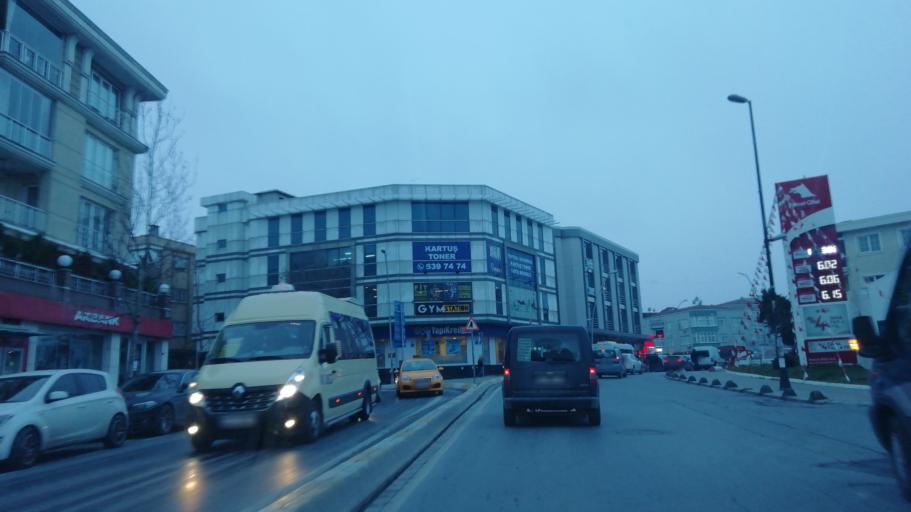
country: TR
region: Istanbul
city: Bahcelievler
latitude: 41.0156
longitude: 28.8248
